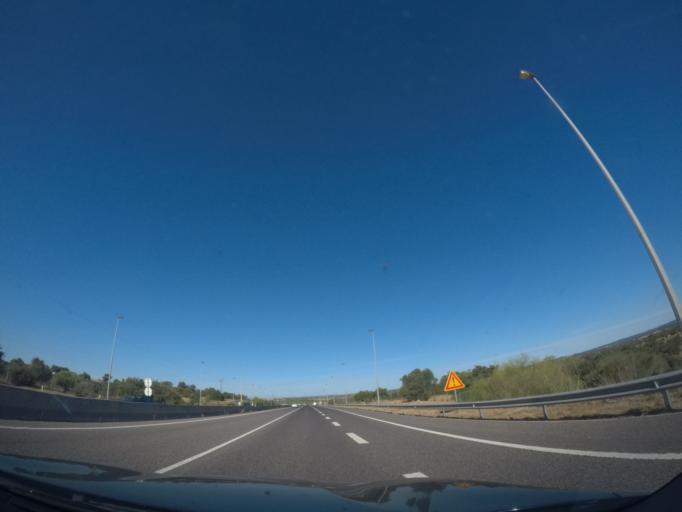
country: PT
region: Faro
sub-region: Portimao
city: Portimao
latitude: 37.1770
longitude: -8.5622
